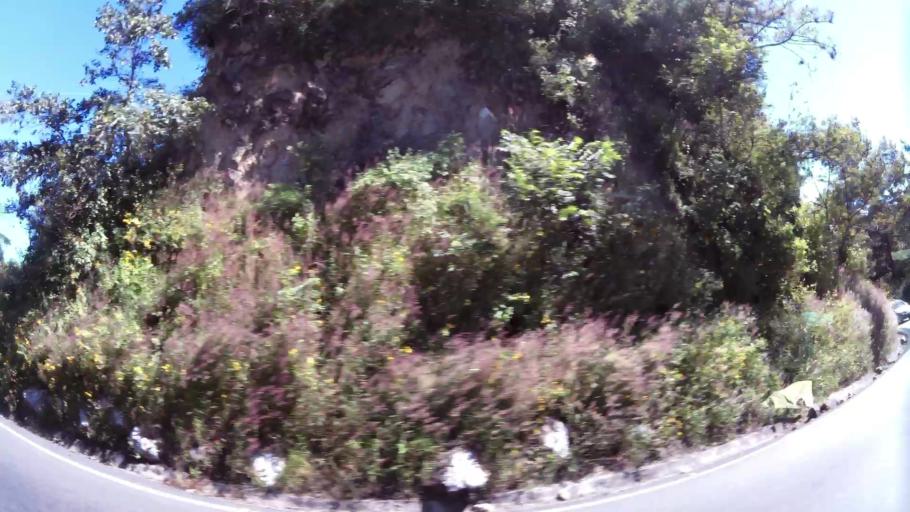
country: GT
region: Solola
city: Solola
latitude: 14.7618
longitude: -91.1776
